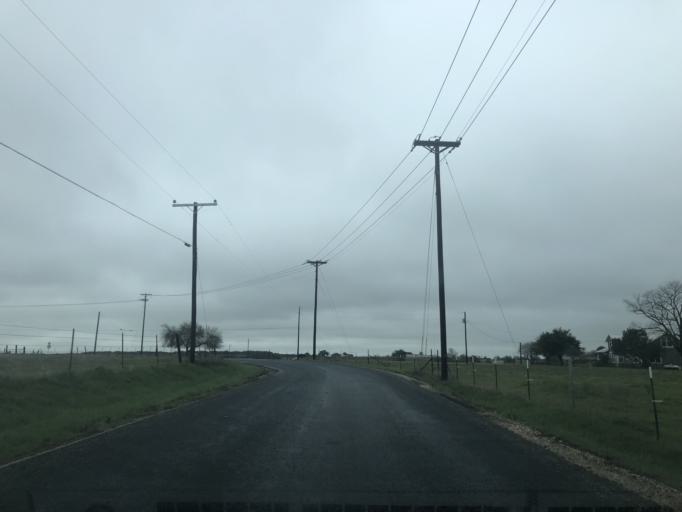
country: US
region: Texas
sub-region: Williamson County
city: Serenada
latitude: 30.7587
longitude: -97.6128
